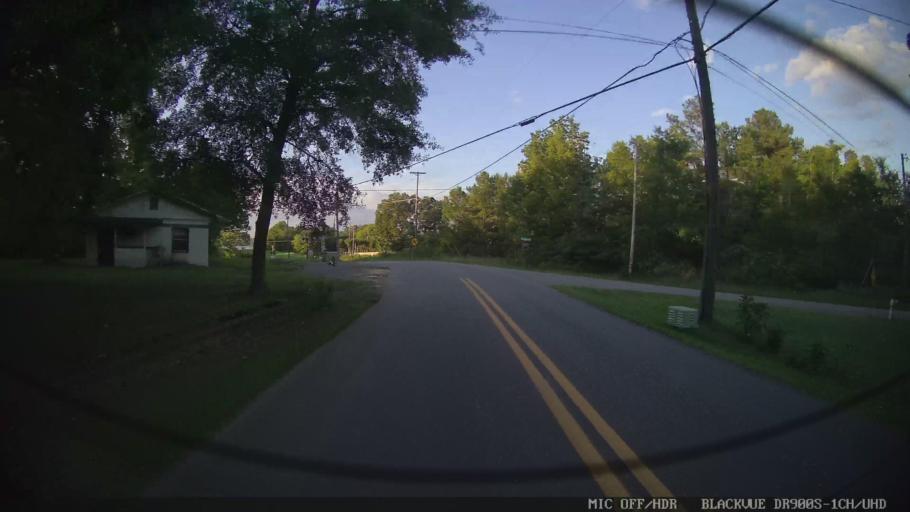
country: US
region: Georgia
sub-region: Bartow County
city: Emerson
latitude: 34.1076
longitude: -84.7122
